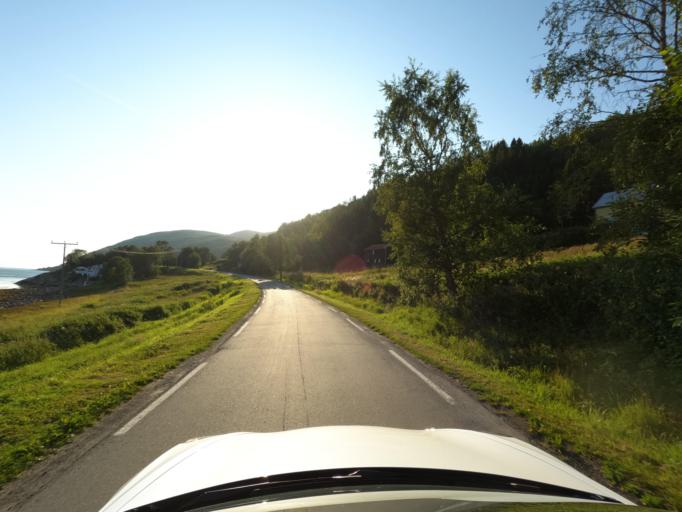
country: NO
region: Nordland
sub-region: Ballangen
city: Ballangen
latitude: 68.4684
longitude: 16.8093
